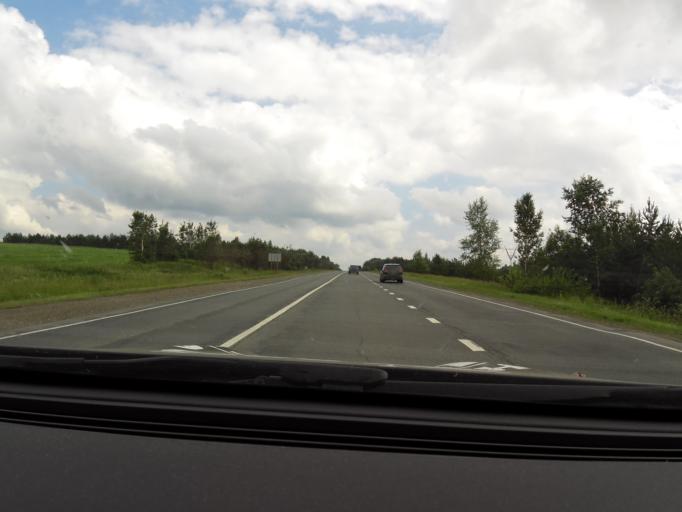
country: RU
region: Sverdlovsk
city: Achit
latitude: 56.8796
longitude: 57.6329
